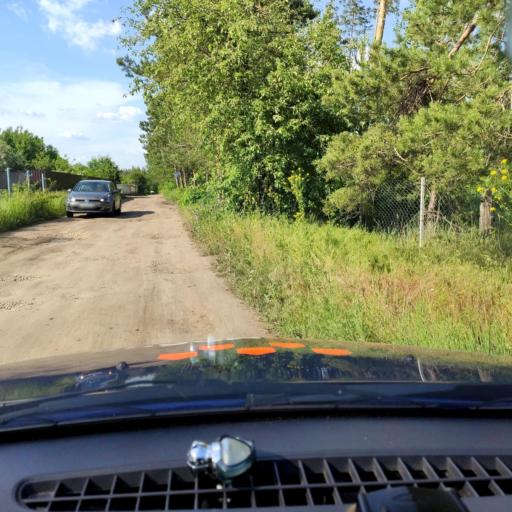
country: RU
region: Voronezj
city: Ramon'
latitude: 51.8923
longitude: 39.2067
